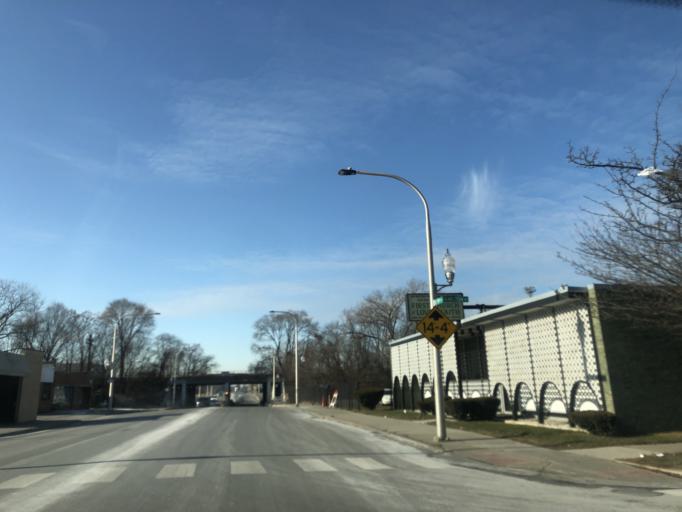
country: US
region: Illinois
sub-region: Cook County
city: Evergreen Park
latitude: 41.7502
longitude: -87.6766
